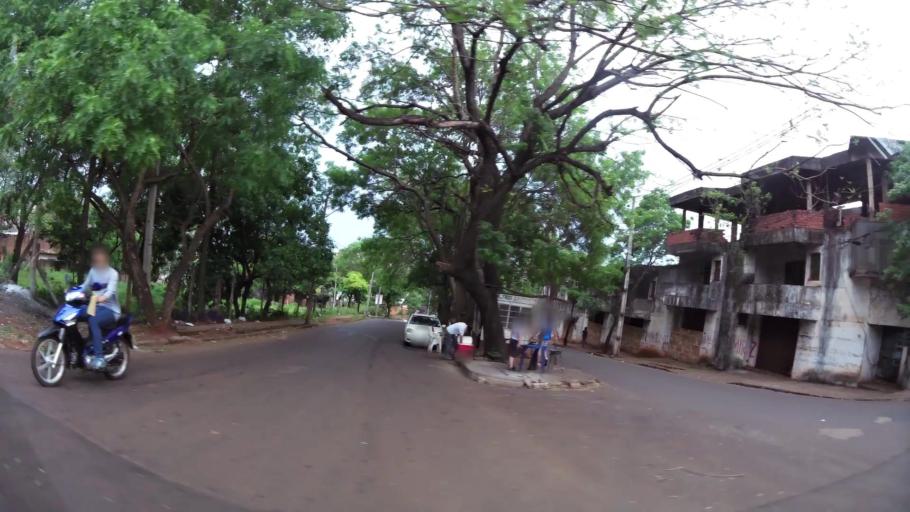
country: PY
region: Alto Parana
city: Ciudad del Este
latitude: -25.5187
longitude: -54.6084
